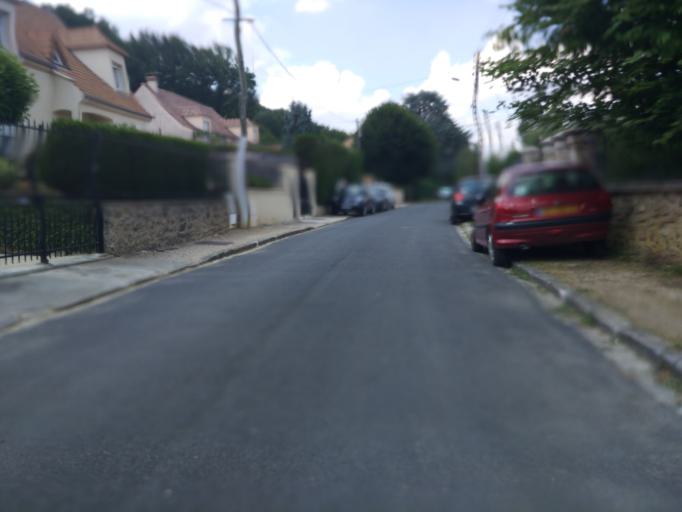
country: FR
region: Ile-de-France
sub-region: Departement des Yvelines
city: Saint-Remy-les-Chevreuse
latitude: 48.6955
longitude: 2.0598
